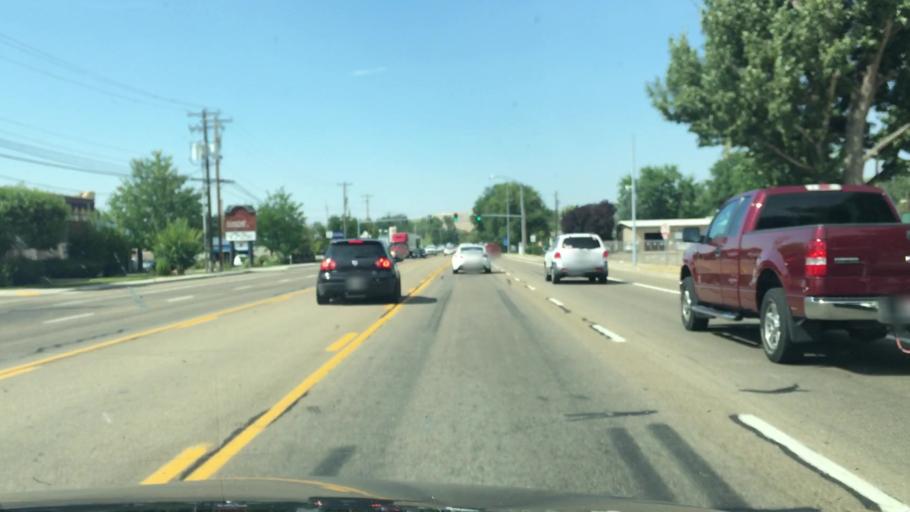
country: US
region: Idaho
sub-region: Ada County
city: Garden City
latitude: 43.6565
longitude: -116.2797
